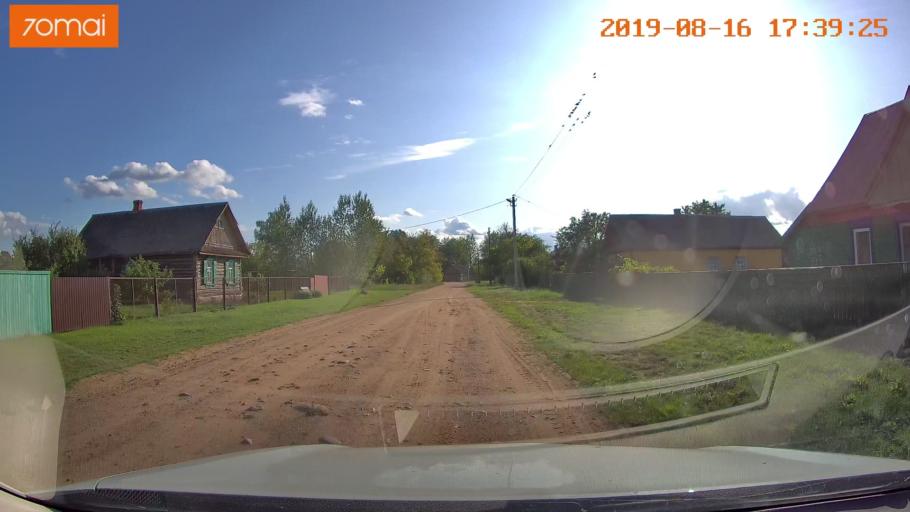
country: BY
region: Mogilev
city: Asipovichy
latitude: 53.2454
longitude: 28.6884
